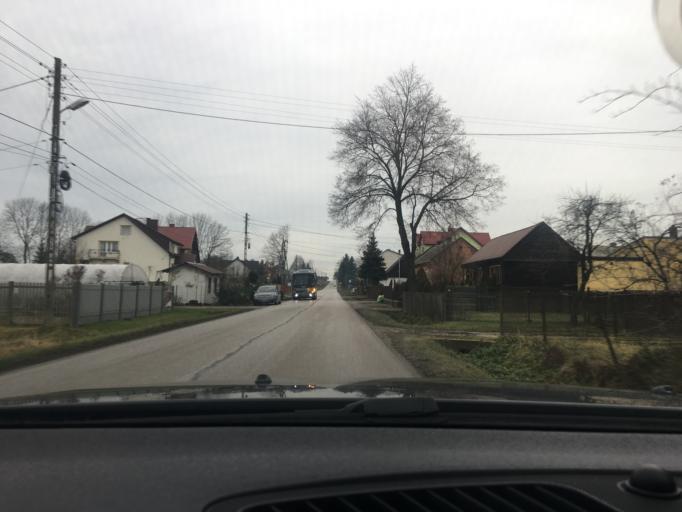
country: PL
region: Swietokrzyskie
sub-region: Powiat jedrzejowski
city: Jedrzejow
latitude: 50.6408
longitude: 20.3567
